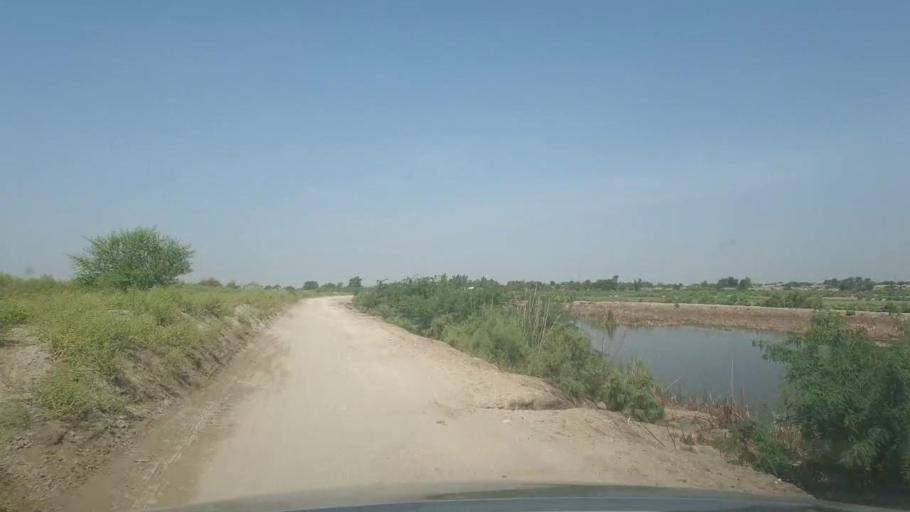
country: PK
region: Sindh
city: Khairpur
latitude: 27.3993
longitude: 69.0503
